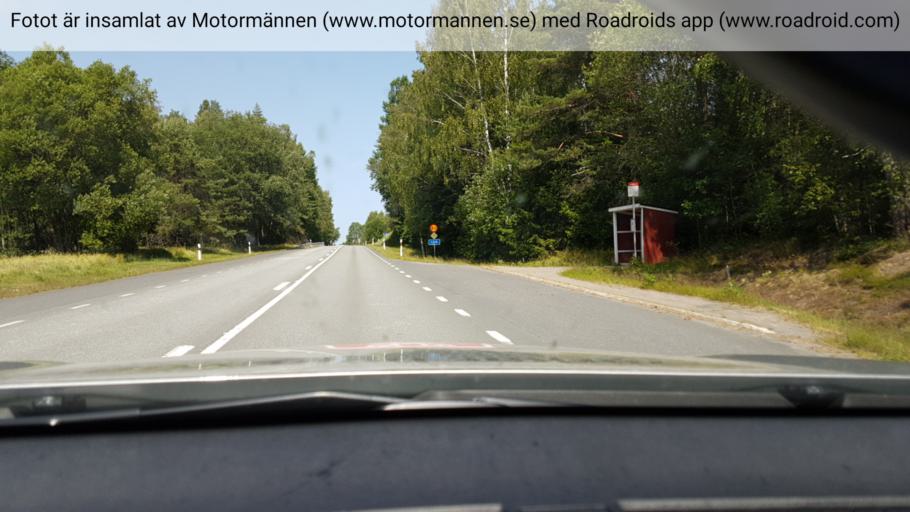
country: SE
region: Joenkoeping
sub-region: Nassjo Kommun
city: Bodafors
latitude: 57.4939
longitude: 14.7960
